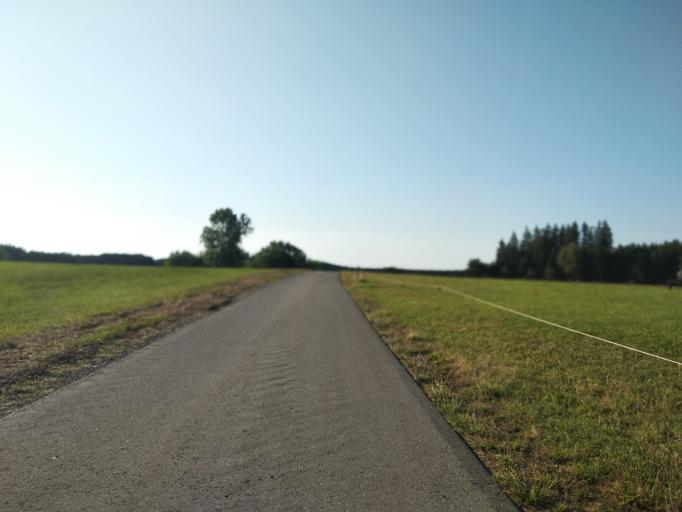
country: DE
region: Bavaria
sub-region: Swabia
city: Legau
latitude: 47.8701
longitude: 10.1131
